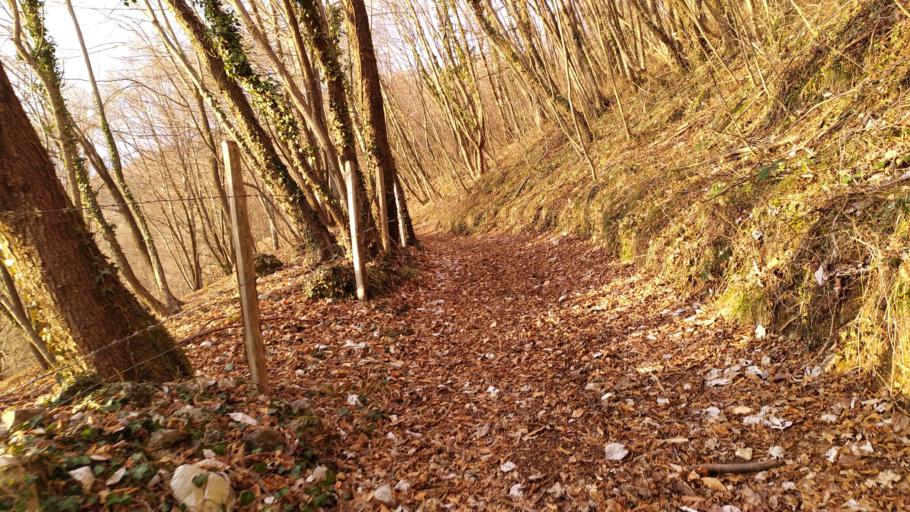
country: IT
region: Veneto
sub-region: Provincia di Vicenza
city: Velo d'Astico
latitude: 45.7642
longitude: 11.3681
